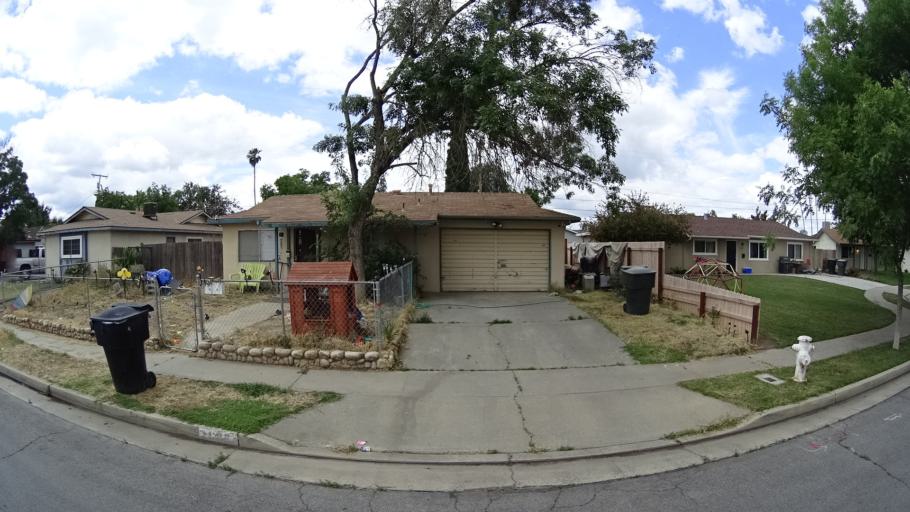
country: US
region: California
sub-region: Kings County
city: Hanford
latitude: 36.3512
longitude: -119.6388
